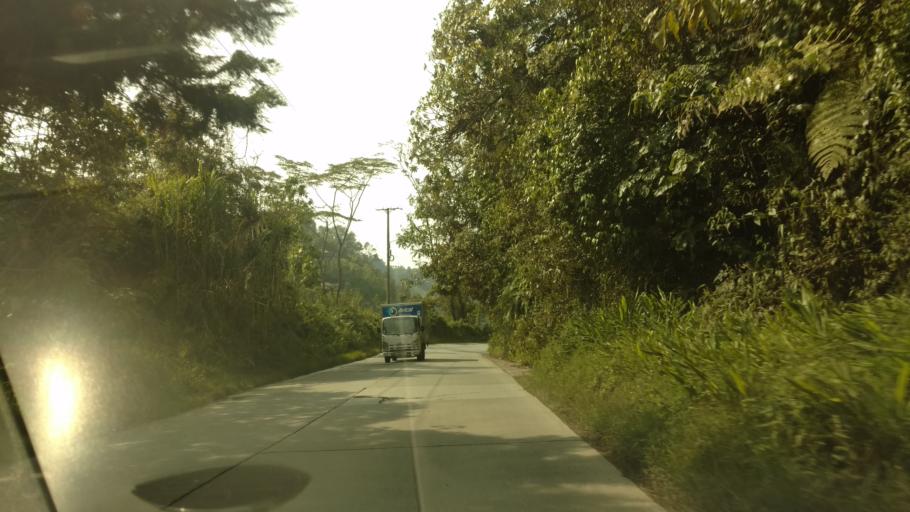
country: CO
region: Caldas
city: Manizales
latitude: 5.0766
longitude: -75.5100
